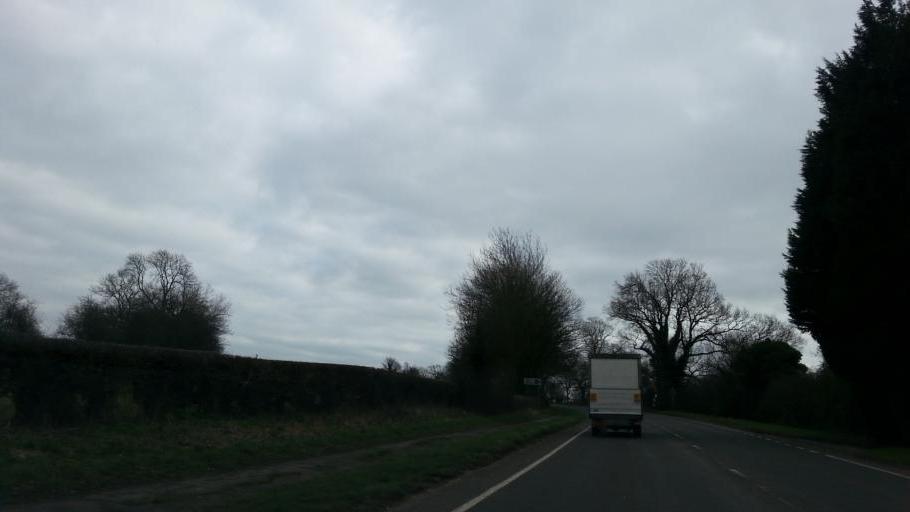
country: GB
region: England
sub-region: Staffordshire
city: Stafford
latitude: 52.8685
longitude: -2.0874
